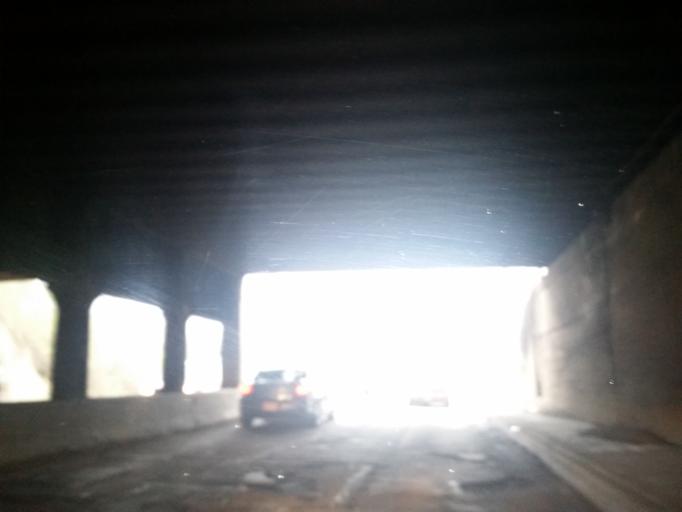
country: US
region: Ohio
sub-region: Cuyahoga County
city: Brooklyn
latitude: 41.4447
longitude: -81.7643
